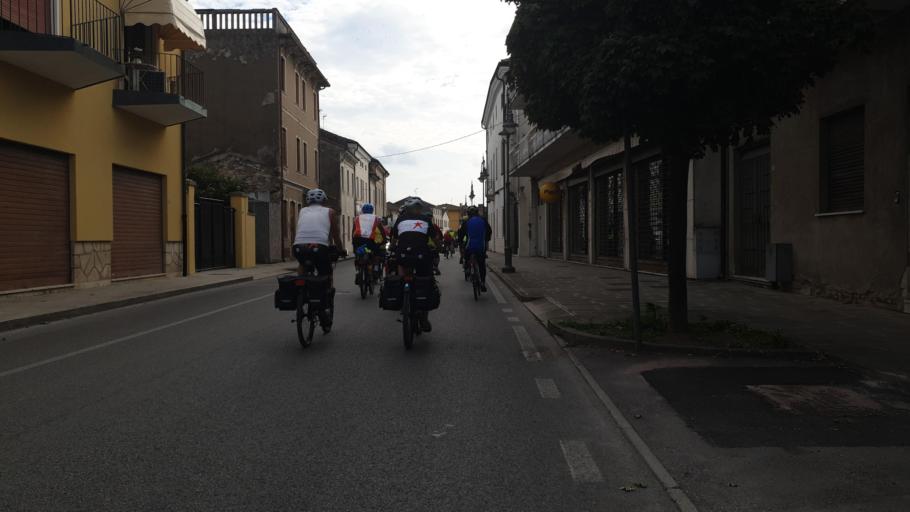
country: IT
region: Veneto
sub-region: Provincia di Vicenza
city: Poiana Maggiore
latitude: 45.2909
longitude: 11.5011
